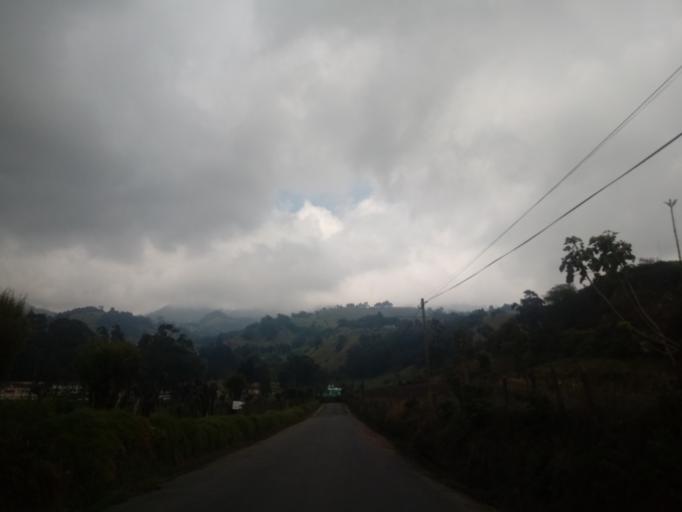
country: CR
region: Cartago
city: Cot
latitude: 9.9290
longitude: -83.8832
